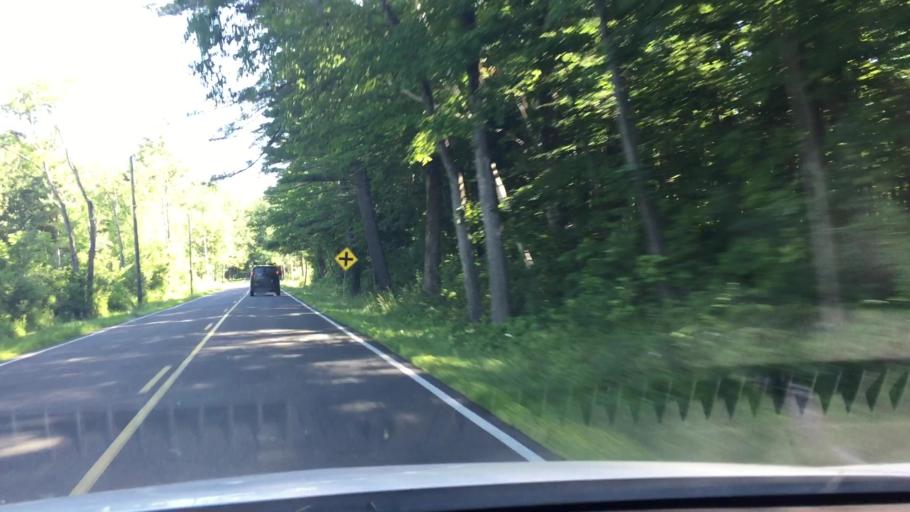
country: US
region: Massachusetts
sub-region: Berkshire County
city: Richmond
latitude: 42.3892
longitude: -73.3395
